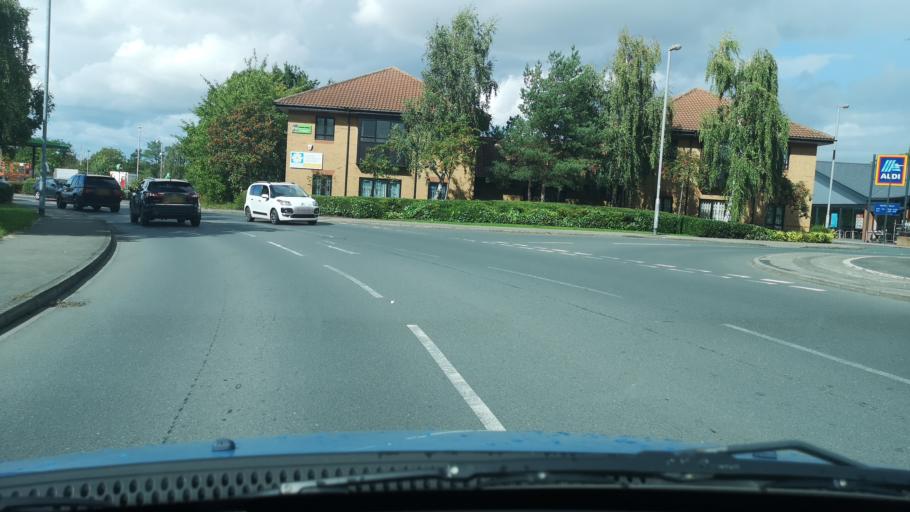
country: GB
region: England
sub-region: City and Borough of Wakefield
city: Crigglestone
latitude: 53.6492
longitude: -1.4981
